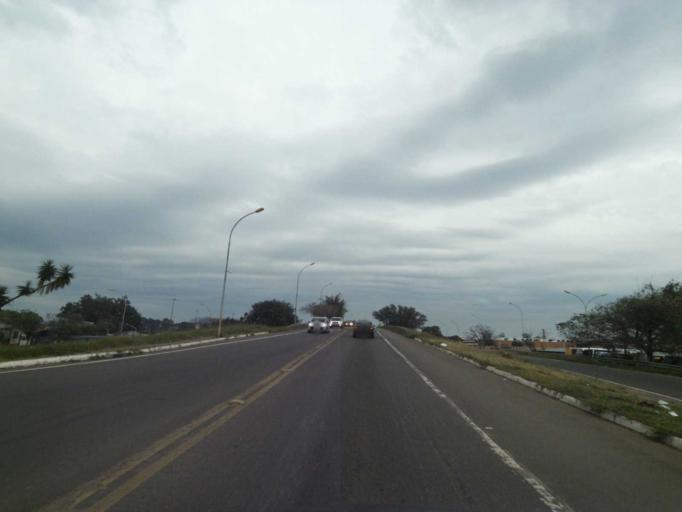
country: BR
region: Rio Grande do Sul
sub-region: Sao Leopoldo
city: Sao Leopoldo
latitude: -29.7608
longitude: -51.1502
